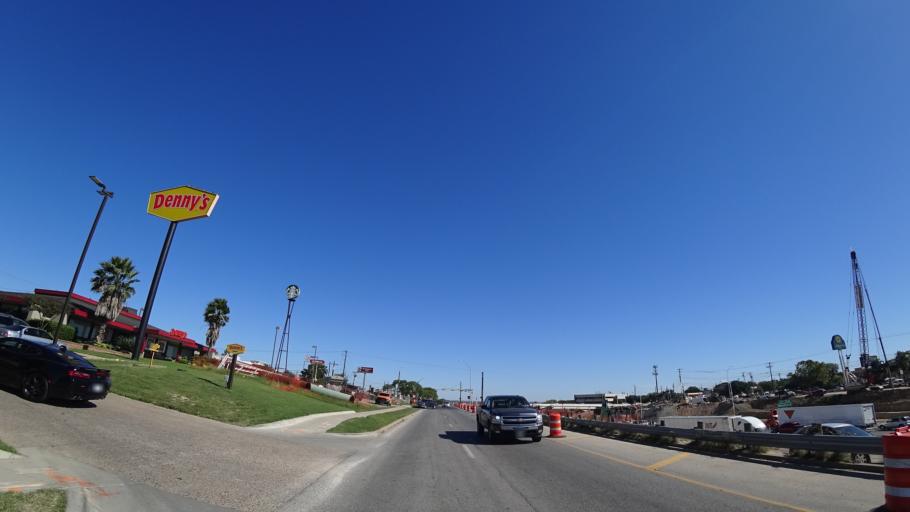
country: US
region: Texas
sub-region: Travis County
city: Austin
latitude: 30.2328
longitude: -97.7423
